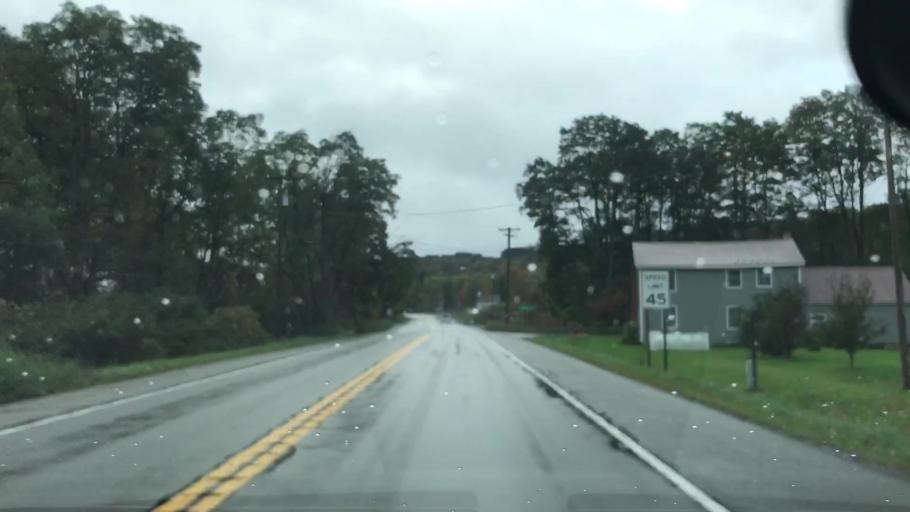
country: US
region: New York
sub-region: Erie County
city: Springville
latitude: 42.4092
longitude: -78.6893
